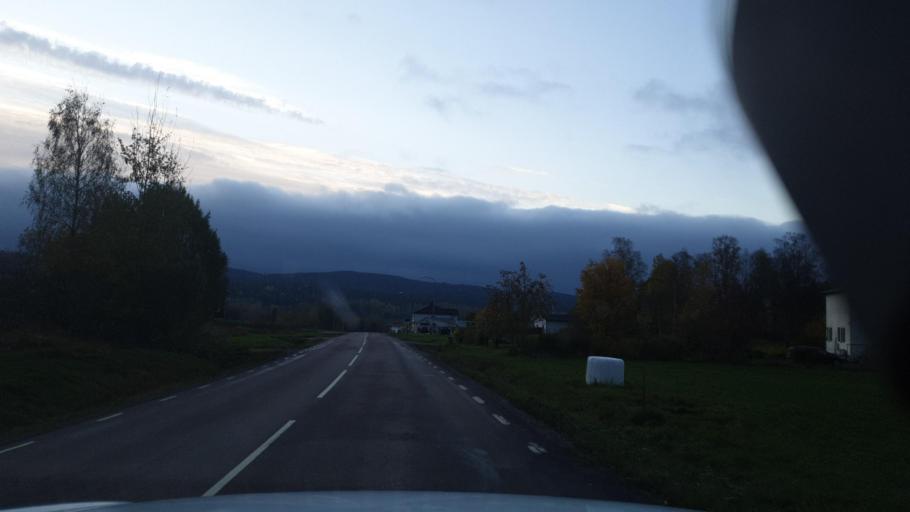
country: SE
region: Vaermland
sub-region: Arvika Kommun
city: Arvika
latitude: 59.7966
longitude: 12.6078
